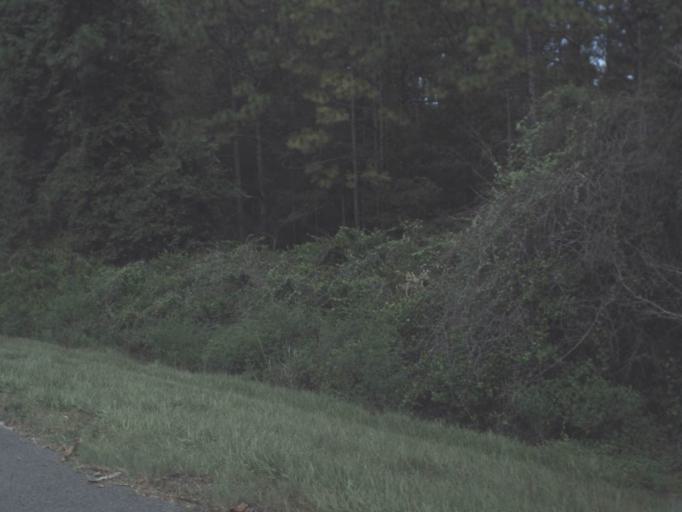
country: US
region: Florida
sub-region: Taylor County
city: Perry
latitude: 30.0996
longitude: -83.6215
